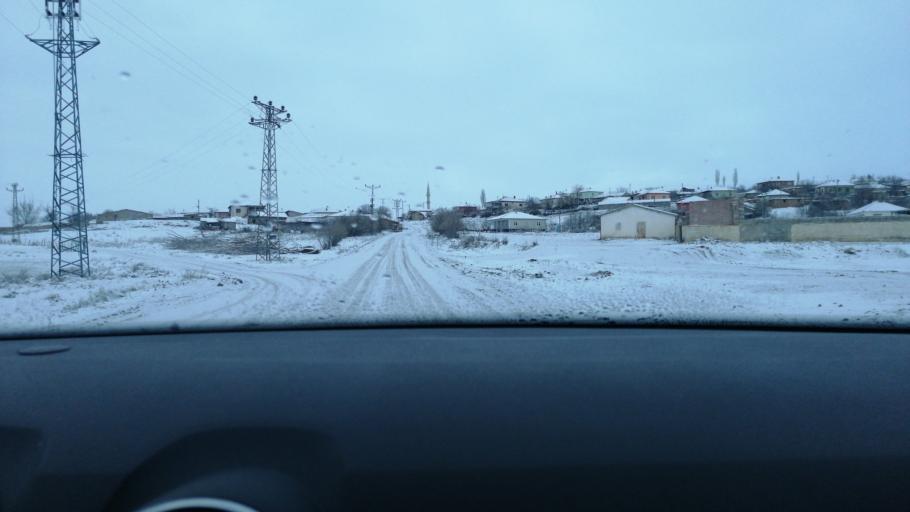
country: TR
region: Aksaray
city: Agacoren
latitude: 38.9377
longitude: 33.9482
